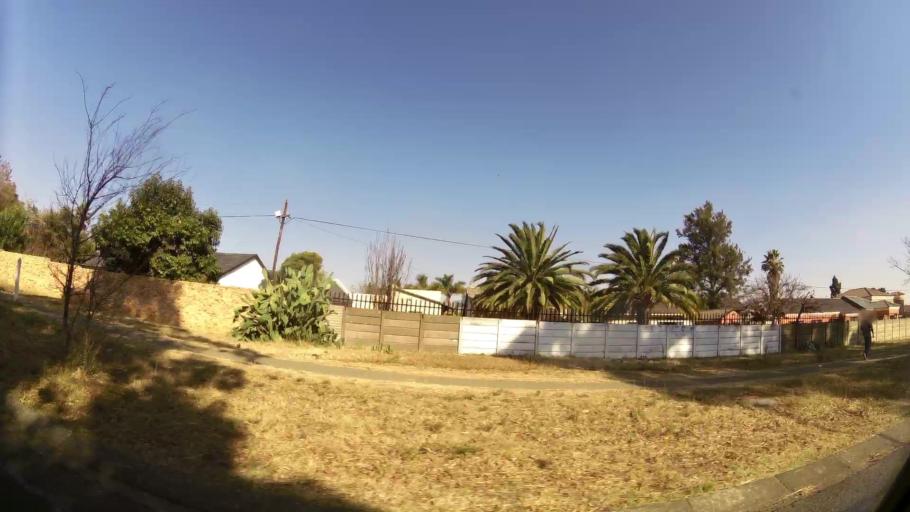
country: ZA
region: Gauteng
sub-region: City of Johannesburg Metropolitan Municipality
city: Johannesburg
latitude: -26.2568
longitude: 28.0027
